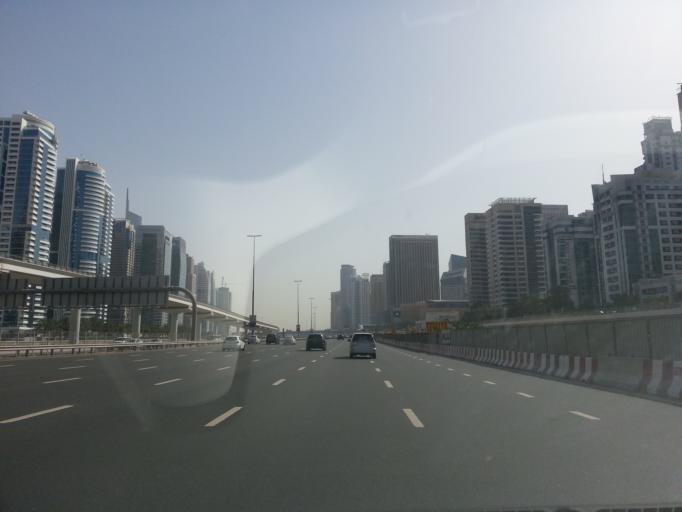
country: AE
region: Dubai
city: Dubai
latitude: 25.0803
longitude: 55.1470
